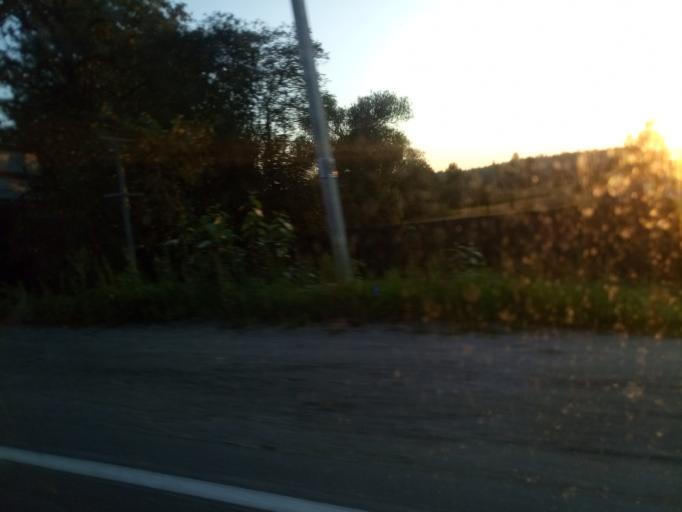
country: RU
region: Moskovskaya
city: Noginsk-9
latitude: 56.0640
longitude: 38.5561
